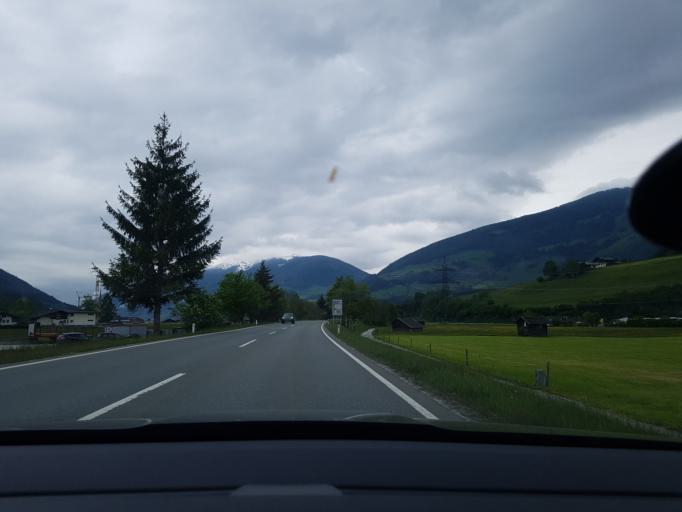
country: AT
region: Salzburg
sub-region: Politischer Bezirk Zell am See
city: Hollersbach im Pinzgau
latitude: 47.2760
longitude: 12.4270
